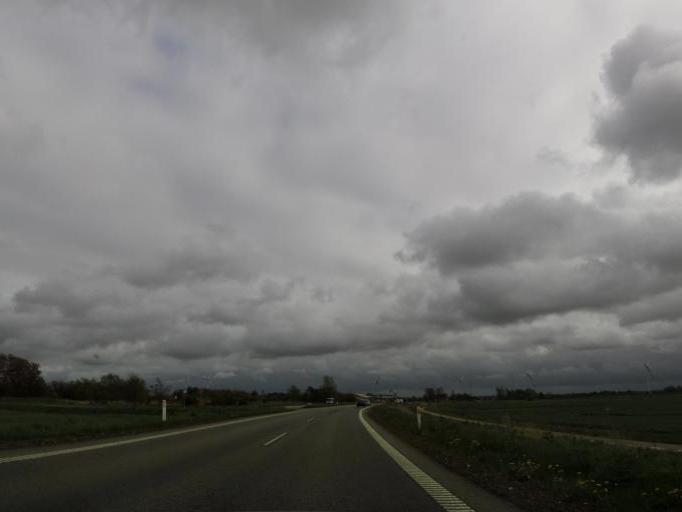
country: DK
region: South Denmark
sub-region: Tonder Kommune
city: Tonder
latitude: 54.9122
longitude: 8.9044
